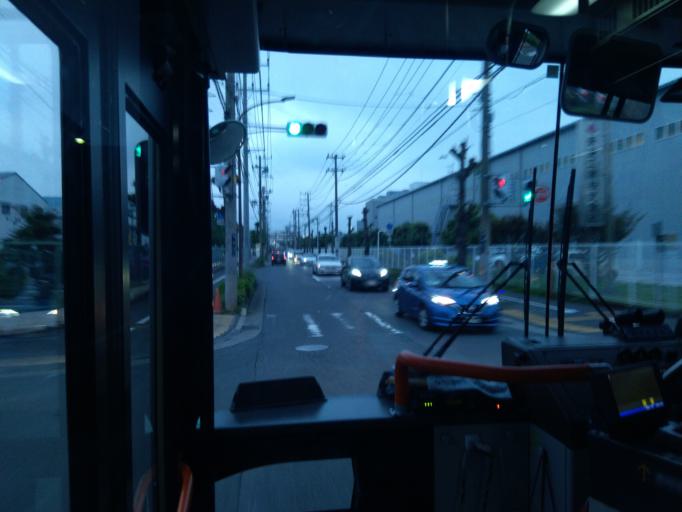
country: JP
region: Kanagawa
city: Hiratsuka
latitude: 35.3397
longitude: 139.3608
